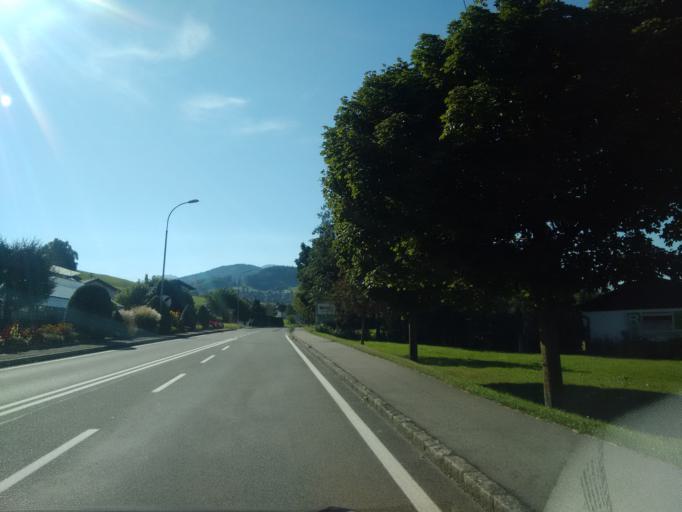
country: AT
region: Upper Austria
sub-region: Politischer Bezirk Vocklabruck
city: Attersee
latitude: 47.9071
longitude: 13.5727
